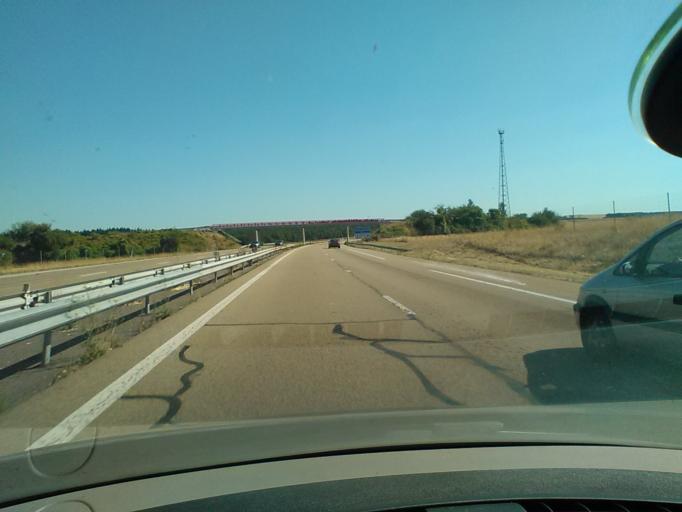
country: FR
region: Bourgogne
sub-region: Departement de l'Yonne
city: Joux-la-Ville
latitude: 47.6473
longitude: 3.9058
